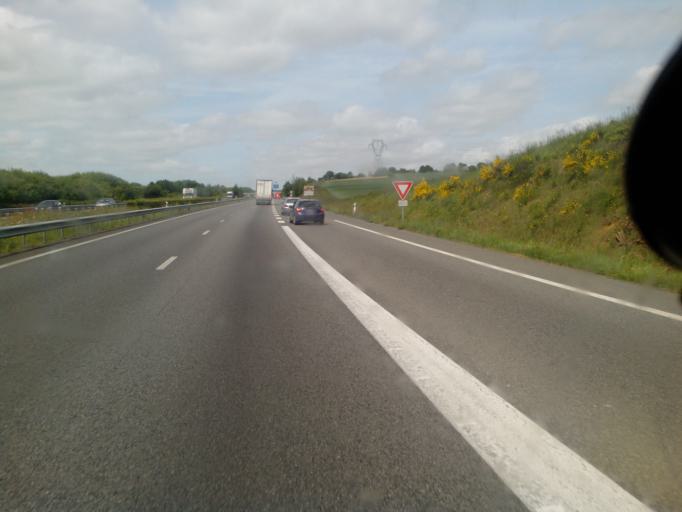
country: FR
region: Brittany
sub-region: Departement d'Ille-et-Vilaine
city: Fouillard
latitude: 48.1420
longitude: -1.5852
